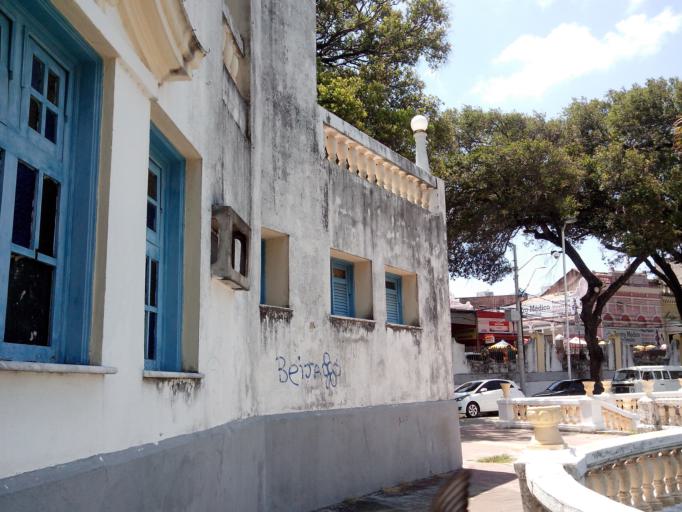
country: BR
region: Ceara
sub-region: Fortaleza
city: Fortaleza
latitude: -3.7316
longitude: -38.5264
